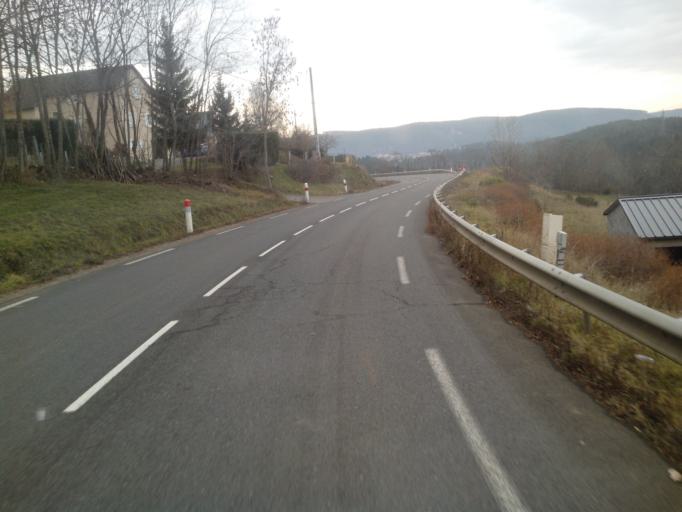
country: FR
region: Languedoc-Roussillon
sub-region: Departement de la Lozere
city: Mende
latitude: 44.5530
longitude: 3.5053
